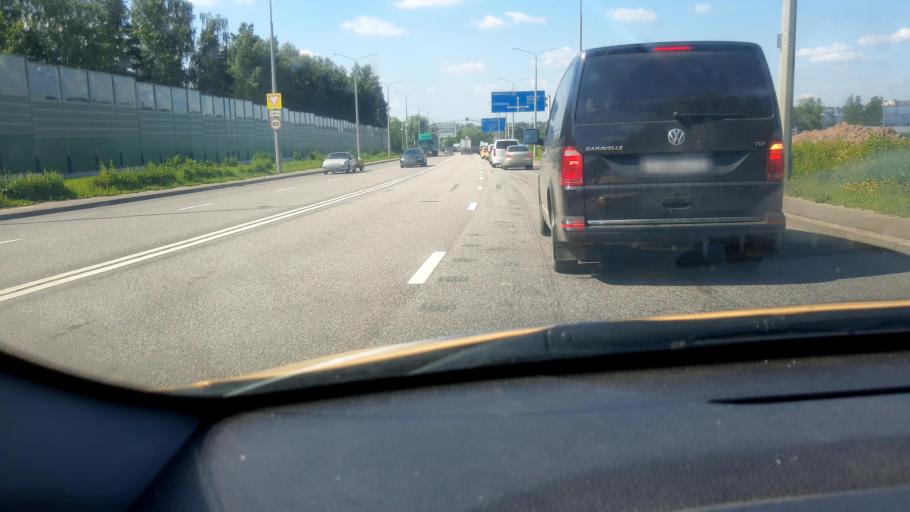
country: RU
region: Moskovskaya
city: Kokoshkino
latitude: 55.5778
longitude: 37.1647
